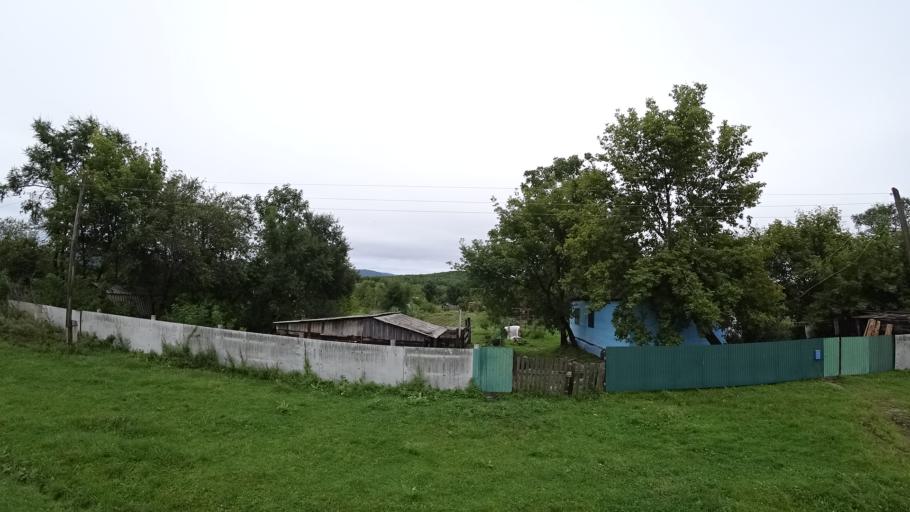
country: RU
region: Primorskiy
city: Monastyrishche
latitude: 44.0834
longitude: 132.5879
